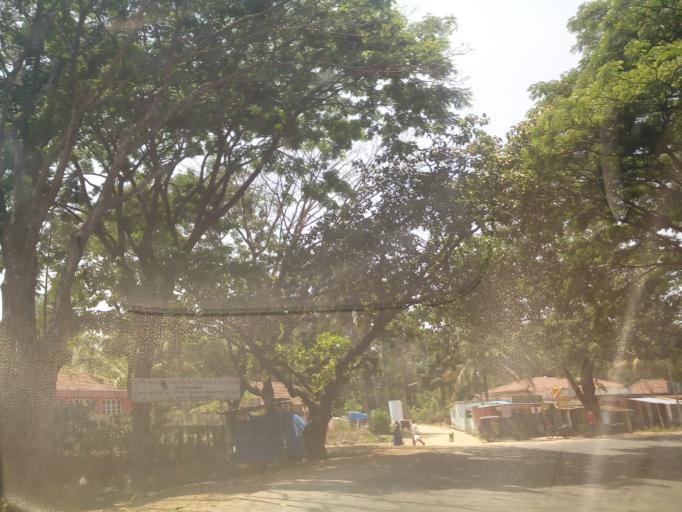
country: IN
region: Karnataka
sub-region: Hassan
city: Sakleshpur
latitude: 12.9476
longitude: 75.8174
